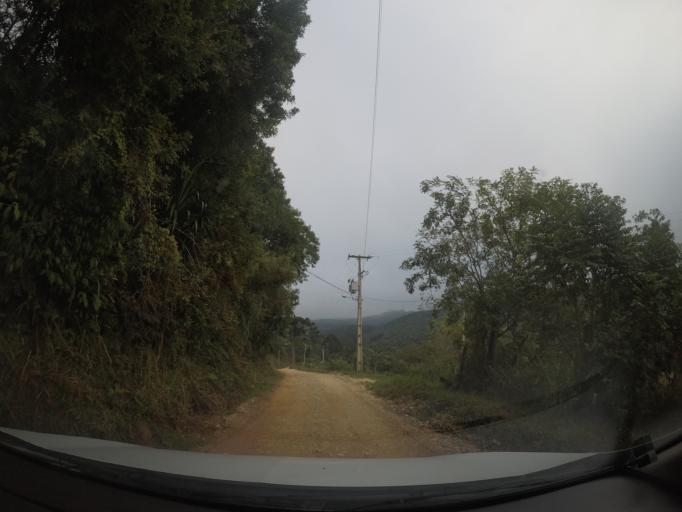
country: BR
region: Parana
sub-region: Colombo
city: Colombo
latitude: -25.3165
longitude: -49.2508
